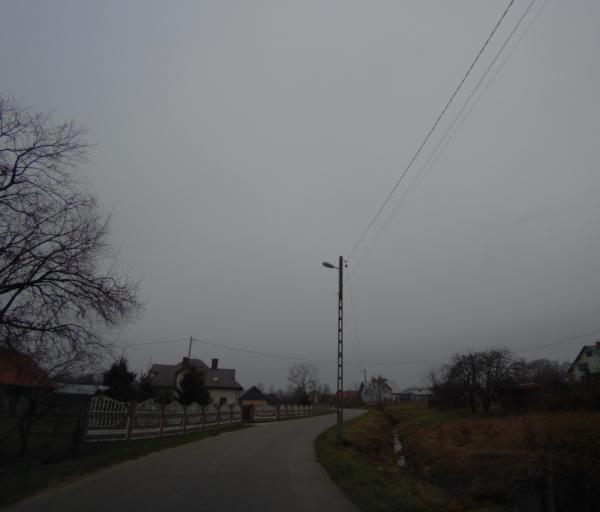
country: PL
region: Subcarpathian Voivodeship
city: Nowa Sarzyna
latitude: 50.2927
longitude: 22.3526
